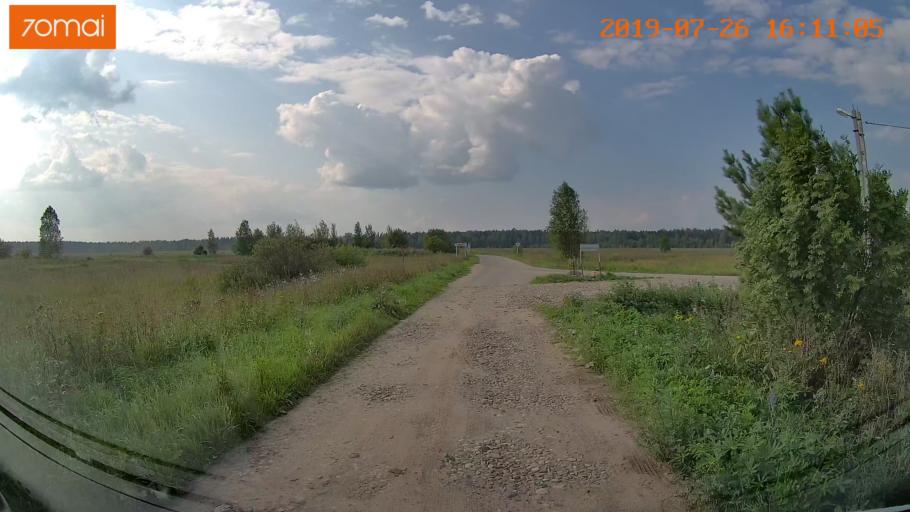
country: RU
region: Ivanovo
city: Bogorodskoye
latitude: 57.0647
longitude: 41.0616
